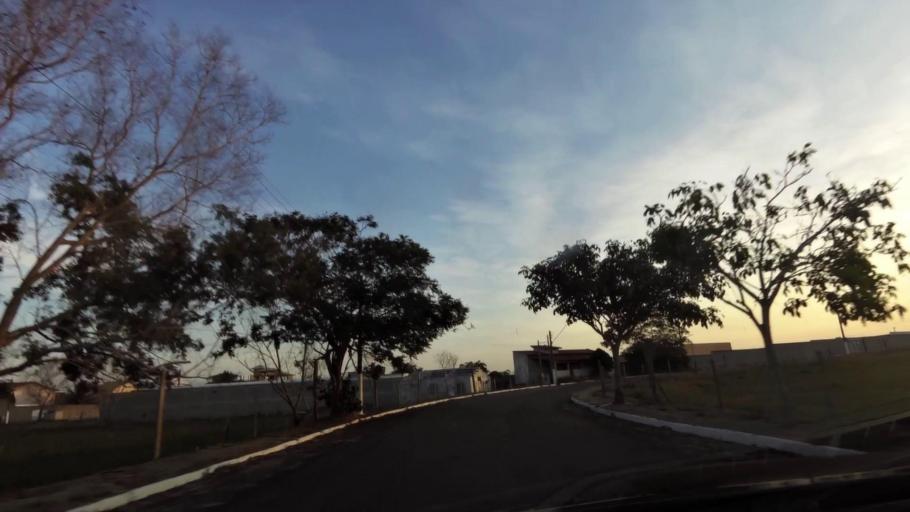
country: BR
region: Espirito Santo
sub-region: Vitoria
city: Vitoria
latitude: -20.4750
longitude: -40.3504
